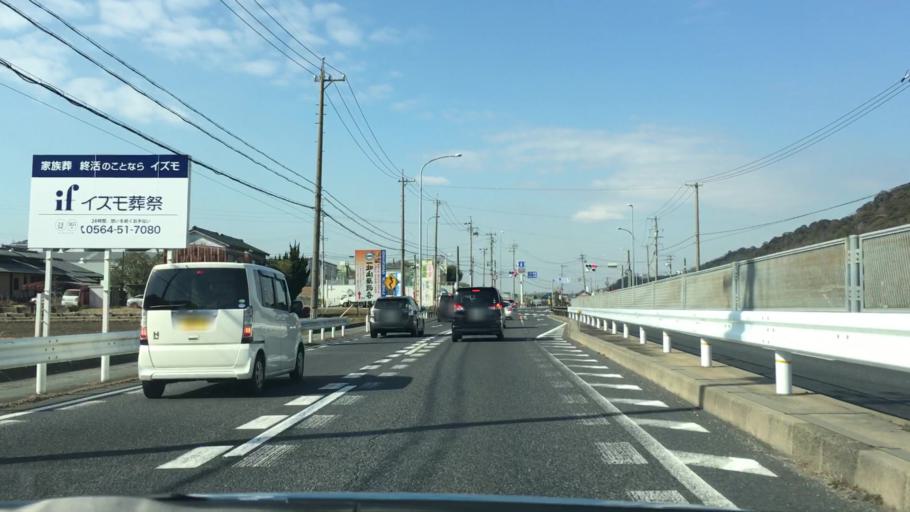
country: JP
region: Aichi
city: Gamagori
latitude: 34.9066
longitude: 137.2319
